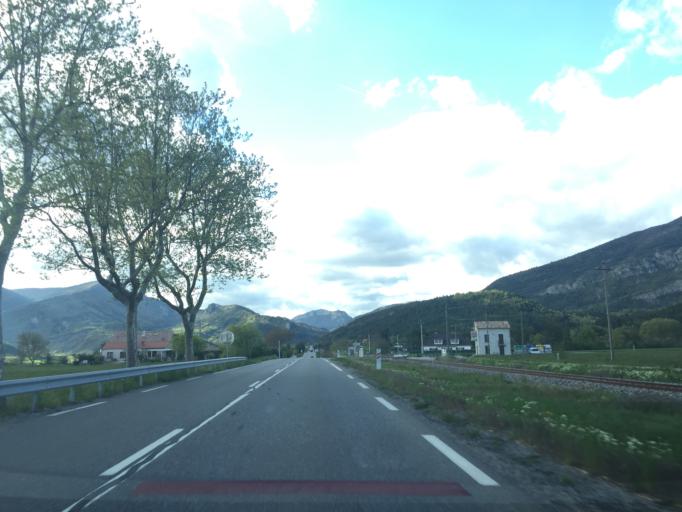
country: FR
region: Provence-Alpes-Cote d'Azur
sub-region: Departement des Hautes-Alpes
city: Serres
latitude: 44.4034
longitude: 5.7316
